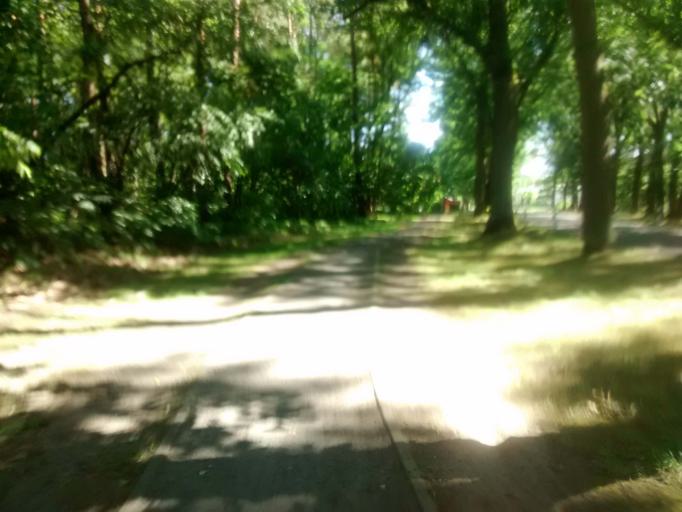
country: DE
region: Brandenburg
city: Hohen Neuendorf
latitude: 52.6827
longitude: 13.2664
